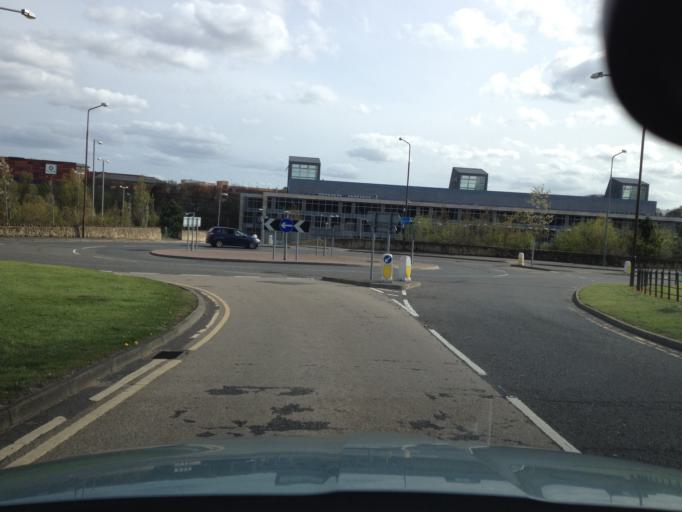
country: GB
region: Scotland
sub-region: West Lothian
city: Livingston
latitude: 55.8886
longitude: -3.5144
